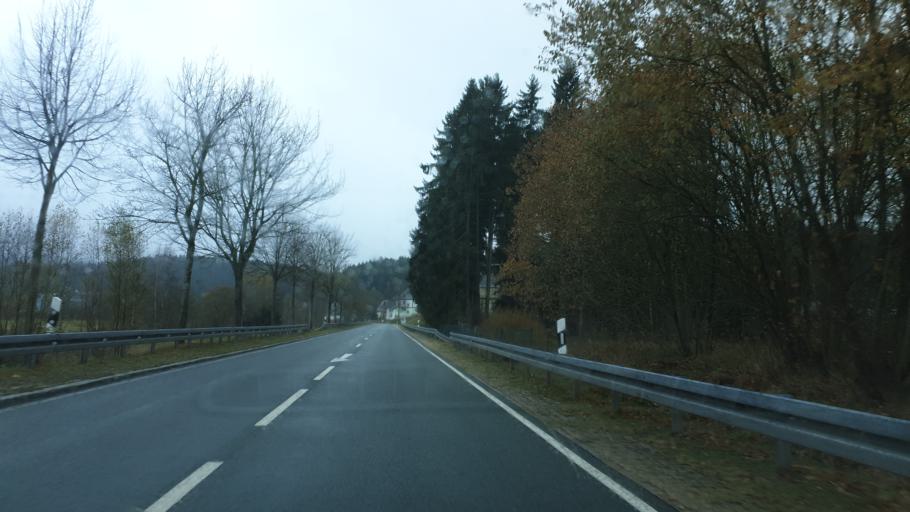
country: DE
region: Saxony
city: Muldenhammer
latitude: 50.4653
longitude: 12.4926
